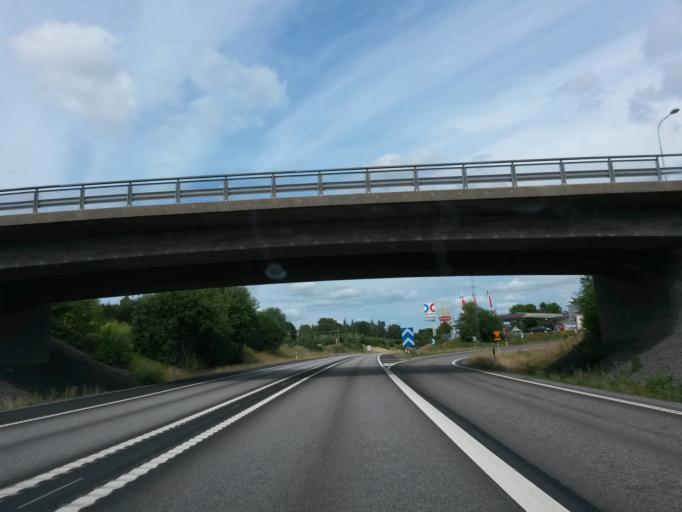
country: SE
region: Vaestra Goetaland
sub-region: Marks Kommun
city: Kinna
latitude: 57.5038
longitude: 12.6959
